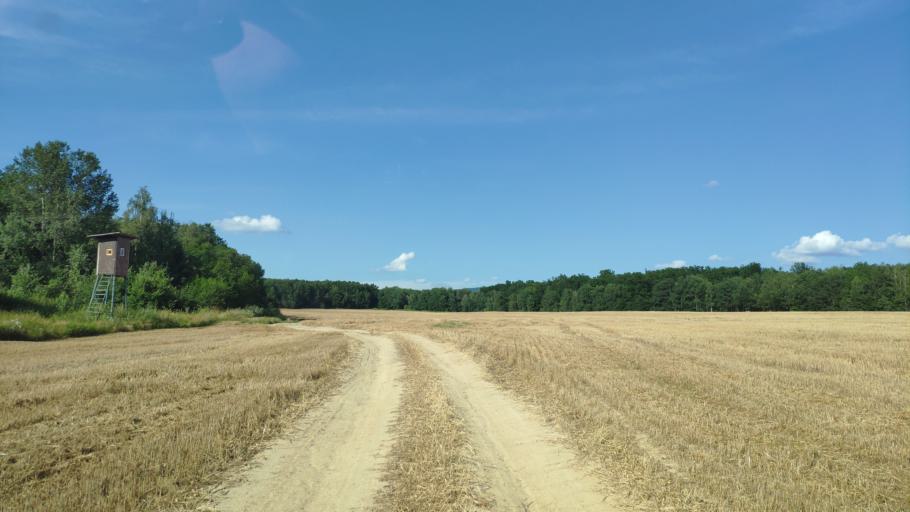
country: SK
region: Presovsky
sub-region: Okres Presov
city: Presov
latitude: 48.9163
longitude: 21.3004
